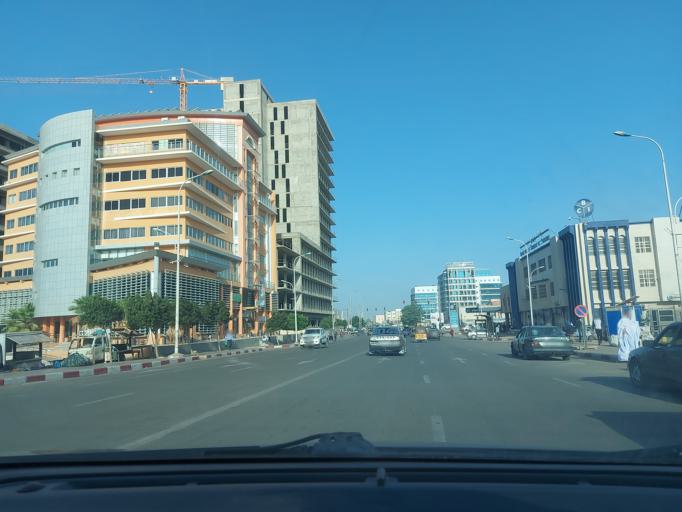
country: MR
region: Nouakchott
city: Nouakchott
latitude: 18.0877
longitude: -15.9764
